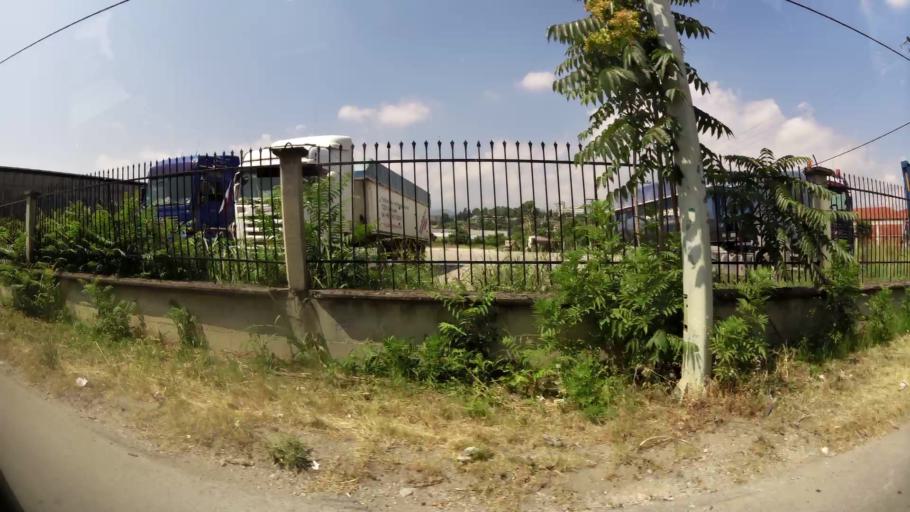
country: GR
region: Central Macedonia
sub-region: Nomos Imathias
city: Veroia
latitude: 40.5266
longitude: 22.2155
